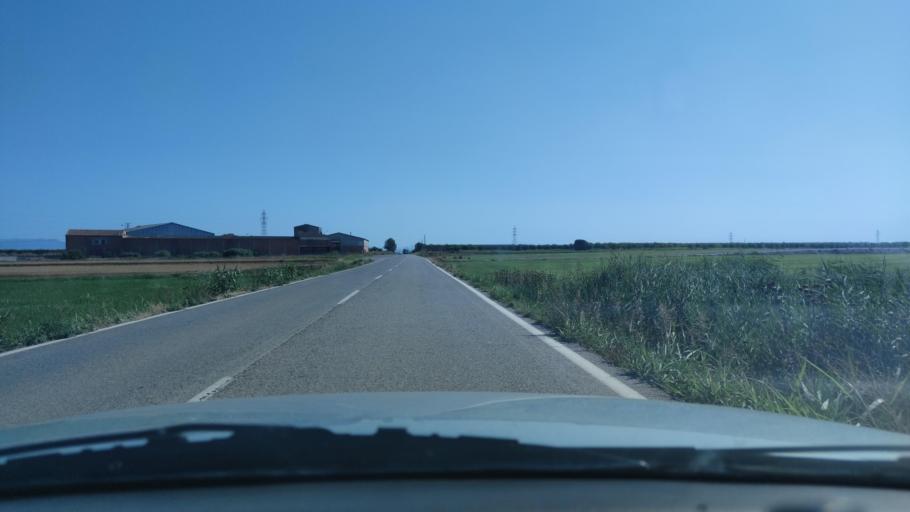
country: ES
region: Catalonia
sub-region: Provincia de Lleida
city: Bellvis
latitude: 41.6470
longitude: 0.7981
